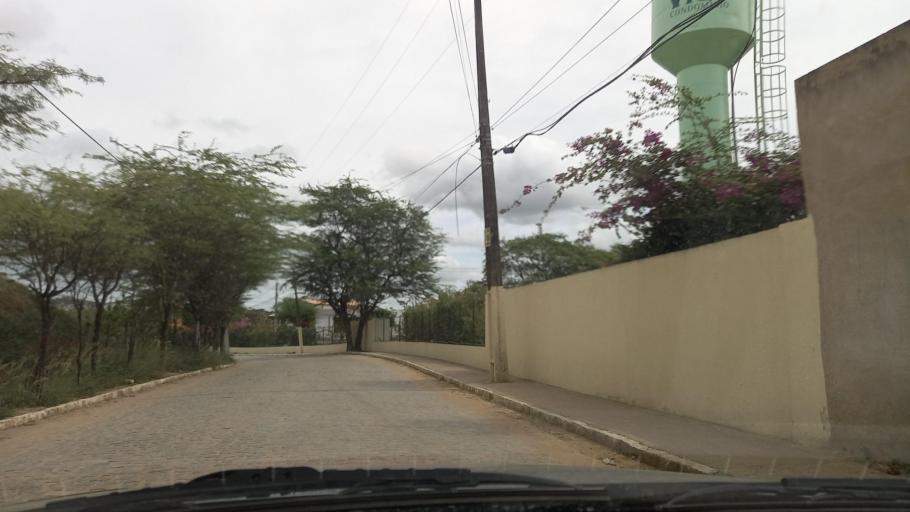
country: BR
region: Pernambuco
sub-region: Gravata
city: Gravata
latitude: -8.1943
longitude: -35.5745
